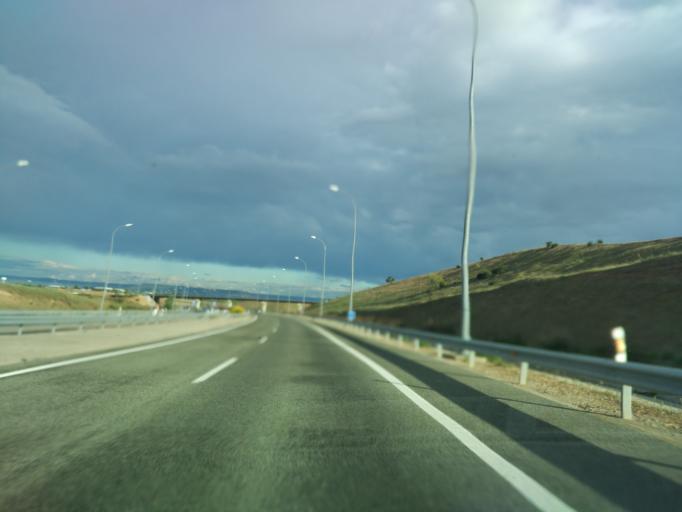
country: ES
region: Madrid
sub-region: Provincia de Madrid
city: Ajalvir
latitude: 40.5123
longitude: -3.4984
